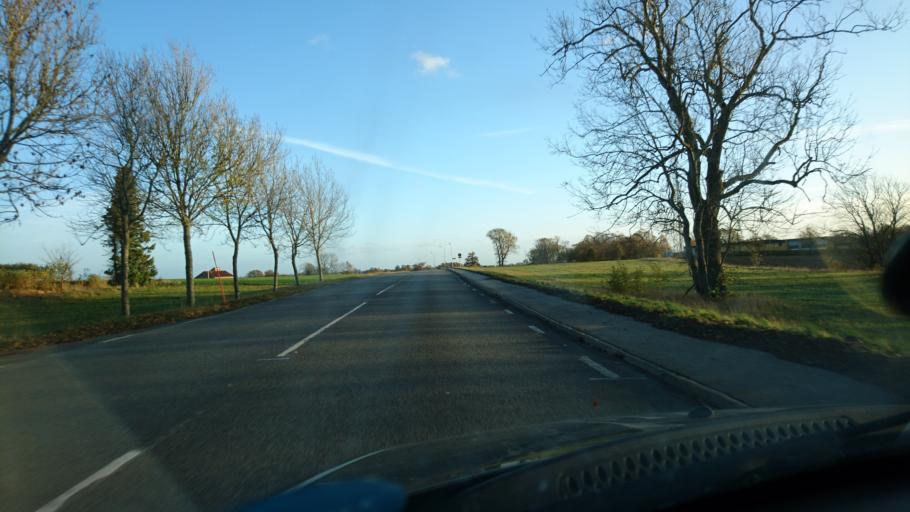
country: SE
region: Skane
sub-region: Simrishamns Kommun
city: Simrishamn
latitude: 55.4647
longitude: 14.1850
